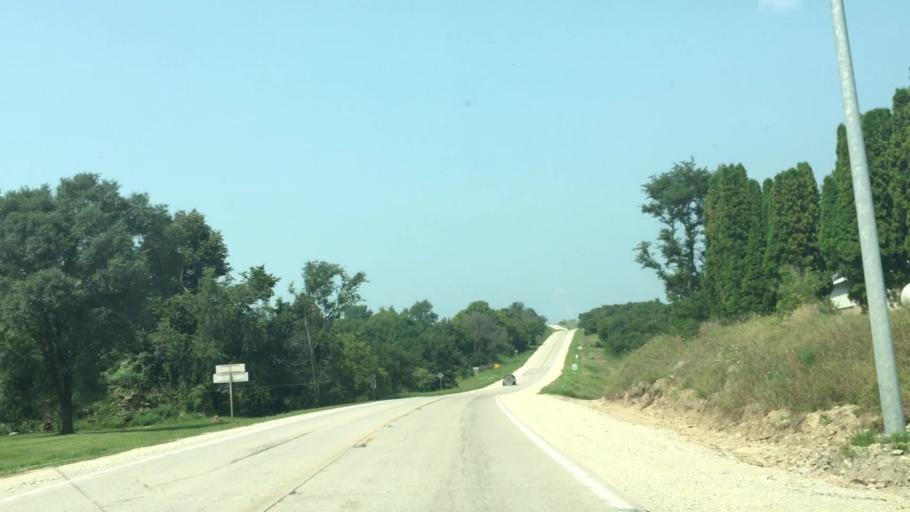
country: US
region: Iowa
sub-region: Fayette County
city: West Union
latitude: 43.1193
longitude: -91.8700
